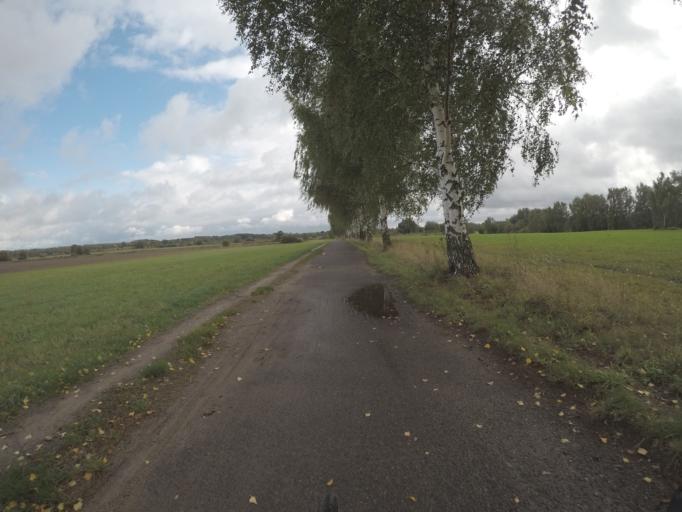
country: DE
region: Berlin
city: Rosenthal
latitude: 52.6140
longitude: 13.3768
